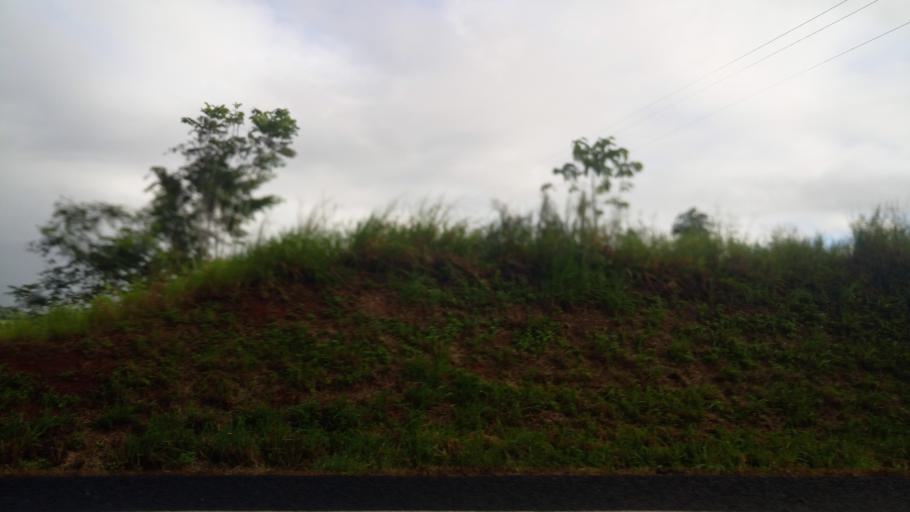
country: AU
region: Queensland
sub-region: Cassowary Coast
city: Innisfail
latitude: -17.5604
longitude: 145.9524
